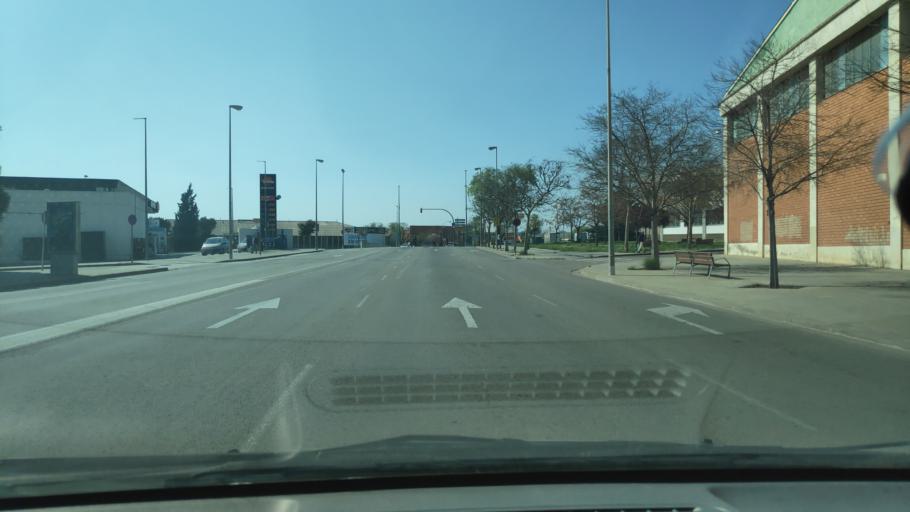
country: ES
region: Catalonia
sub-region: Provincia de Barcelona
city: Sabadell
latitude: 41.5325
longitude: 2.1055
